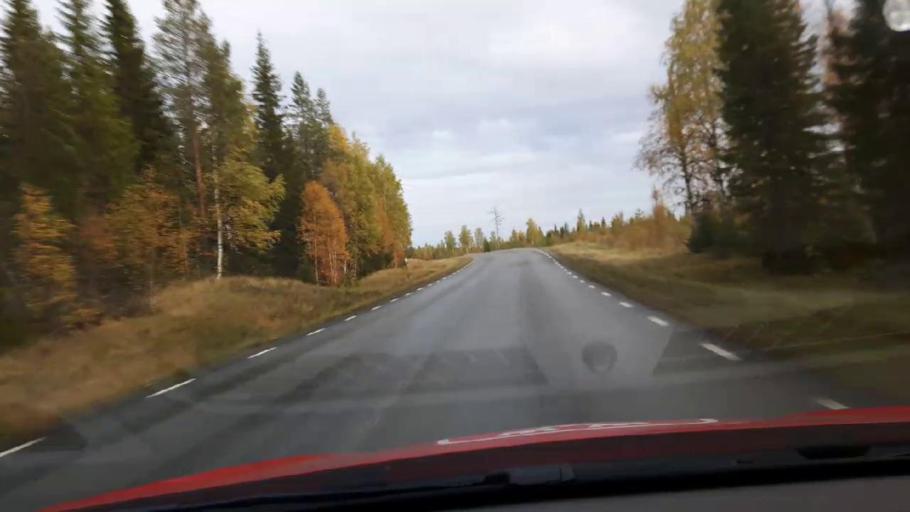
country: SE
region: Jaemtland
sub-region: OEstersunds Kommun
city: Lit
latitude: 63.3164
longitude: 15.0914
